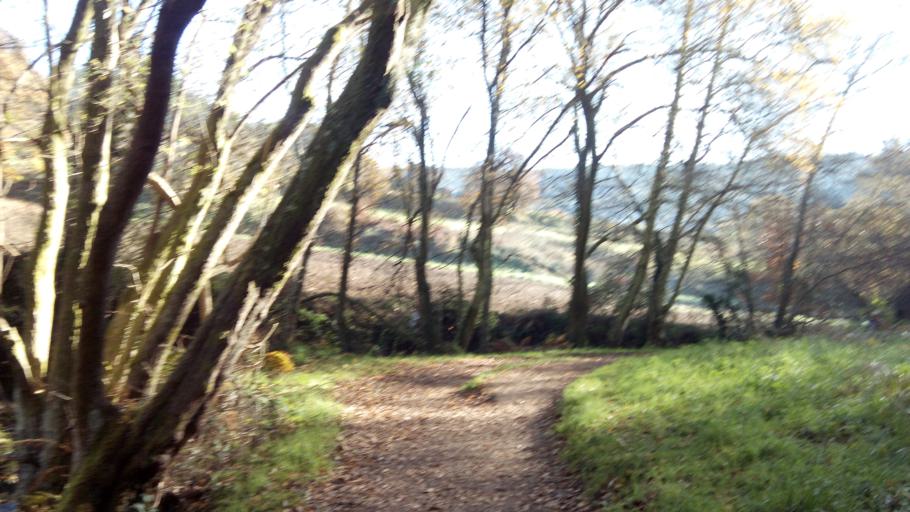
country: ES
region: Galicia
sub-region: Provincia de Pontevedra
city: Meis
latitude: 42.4823
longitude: -8.7417
